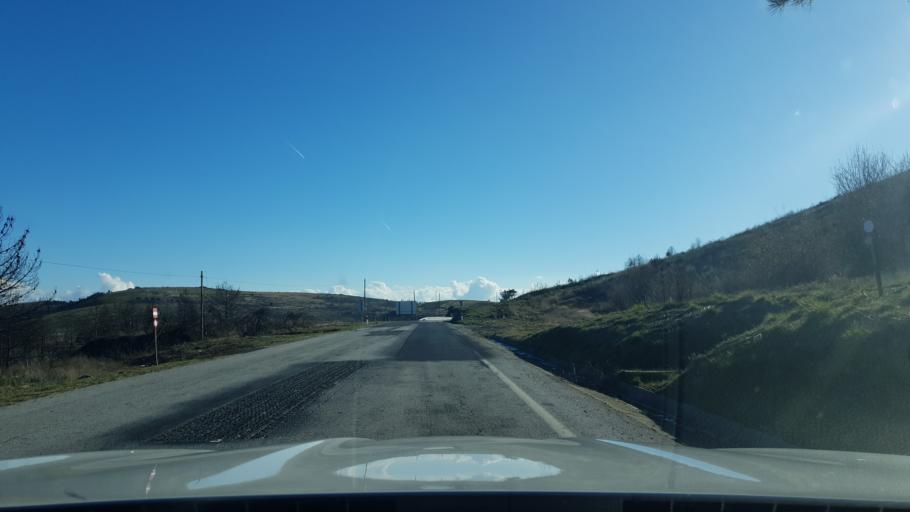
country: PT
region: Braganca
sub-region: Freixo de Espada A Cinta
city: Freixo de Espada a Cinta
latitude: 41.1743
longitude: -6.7909
